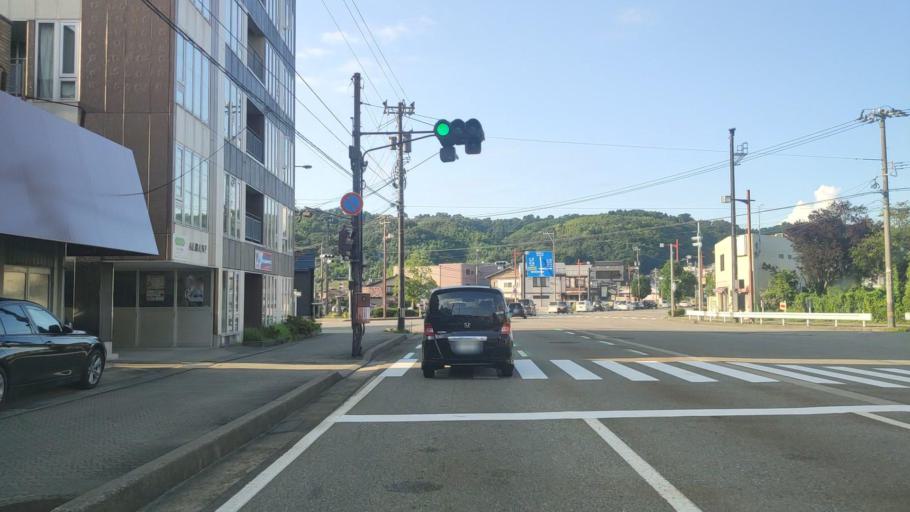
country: JP
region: Ishikawa
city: Kanazawa-shi
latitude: 36.5603
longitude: 136.6774
